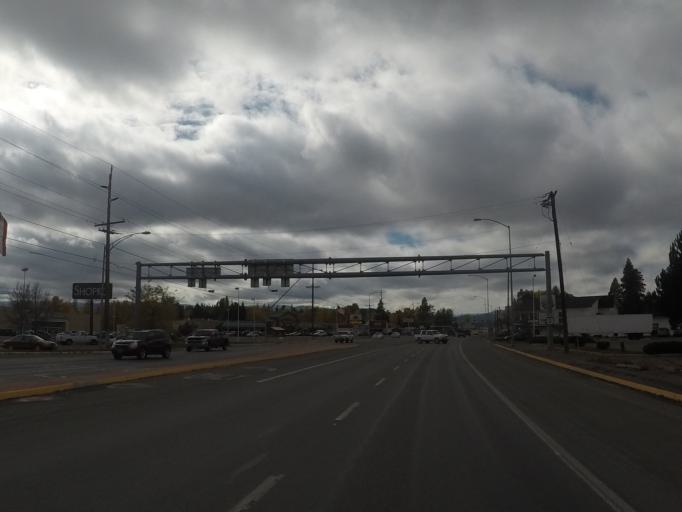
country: US
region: Montana
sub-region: Flathead County
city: Evergreen
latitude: 48.2141
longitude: -114.2779
